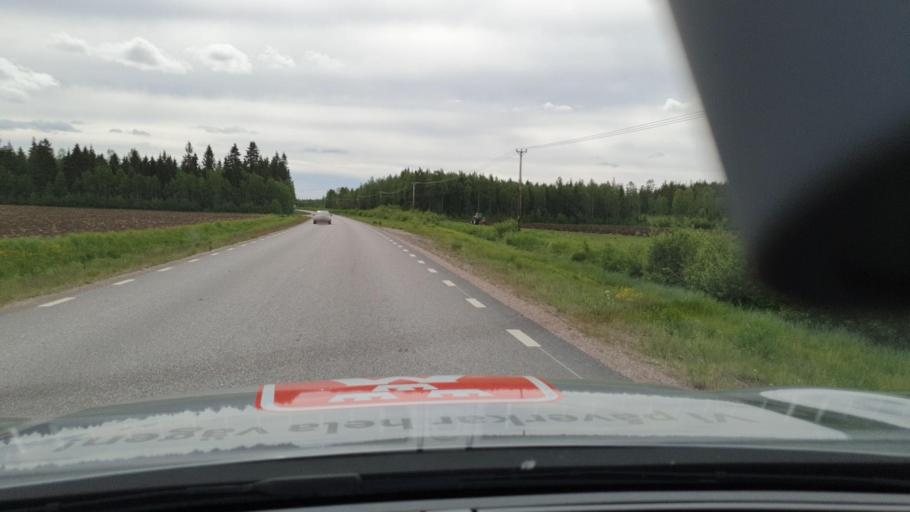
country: SE
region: Norrbotten
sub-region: Kalix Kommun
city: Kalix
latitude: 65.8976
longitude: 23.4618
